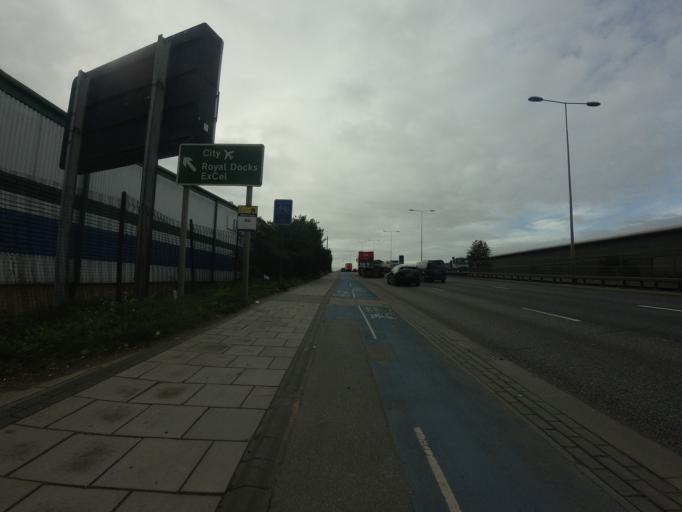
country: GB
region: England
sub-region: Greater London
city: Barking
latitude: 51.5281
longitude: 0.0826
